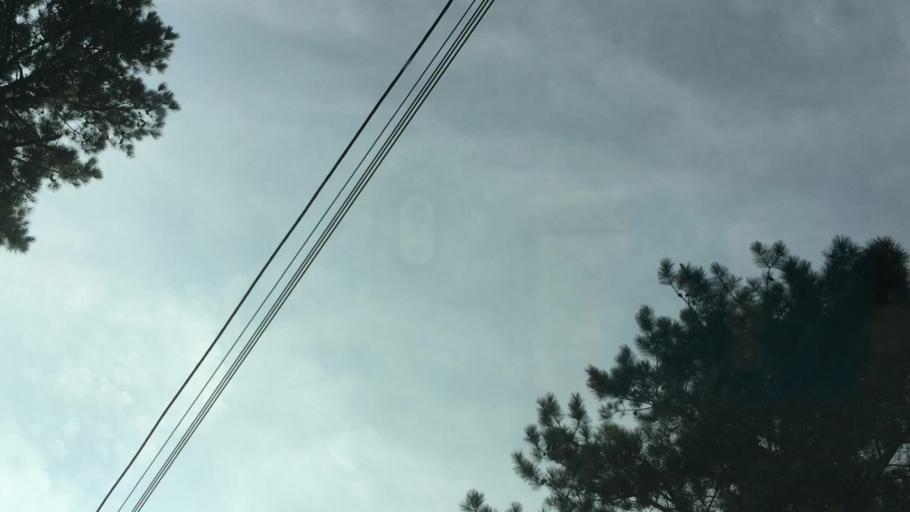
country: US
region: Alabama
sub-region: Bibb County
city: Woodstock
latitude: 33.2270
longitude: -87.1303
